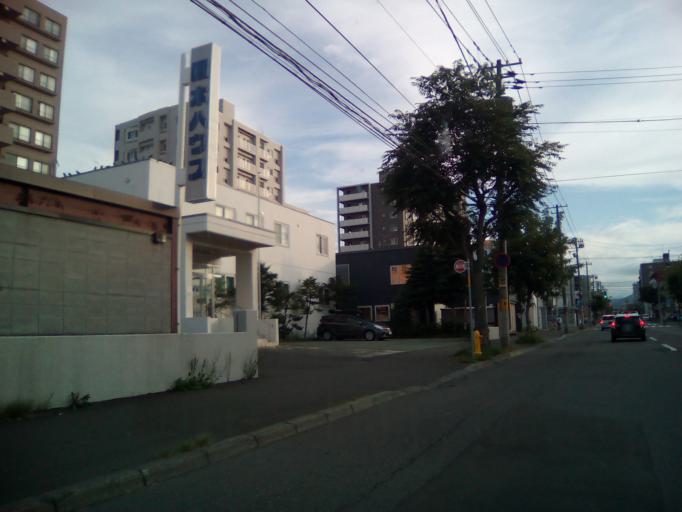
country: JP
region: Hokkaido
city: Sapporo
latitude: 43.0486
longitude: 141.3802
